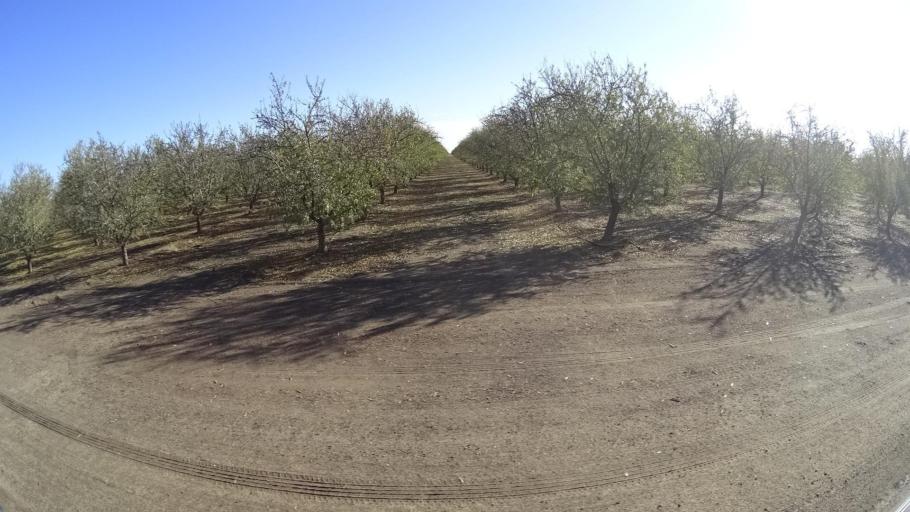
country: US
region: California
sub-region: Kern County
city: Delano
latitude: 35.7242
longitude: -119.3119
